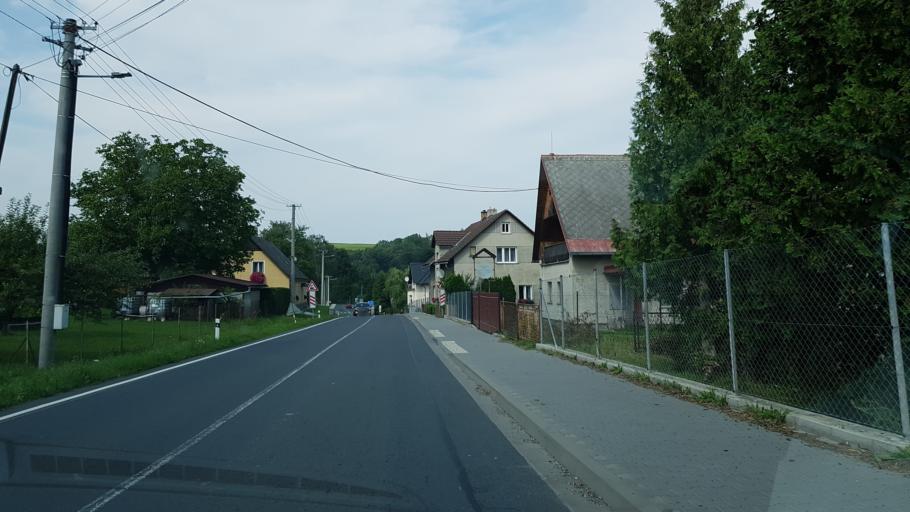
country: CZ
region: Olomoucky
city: Mikulovice
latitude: 50.3005
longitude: 17.3306
